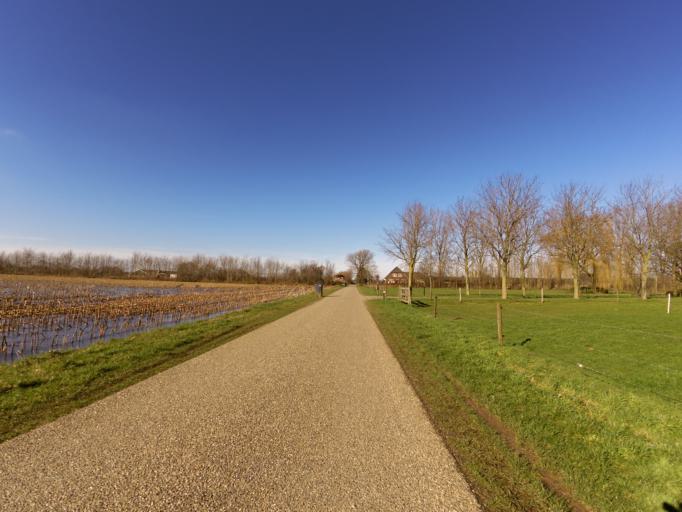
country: NL
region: Gelderland
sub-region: Gemeente Doetinchem
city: Doetinchem
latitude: 51.9600
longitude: 6.2394
